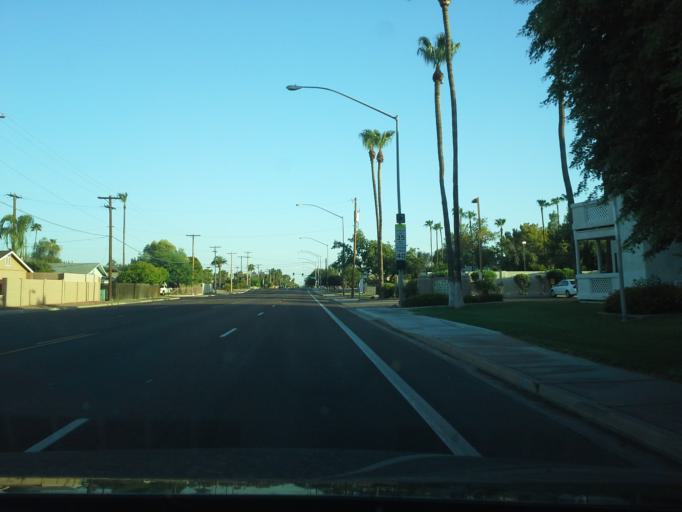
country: US
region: Arizona
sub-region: Maricopa County
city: Mesa
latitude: 33.4324
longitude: -111.8228
